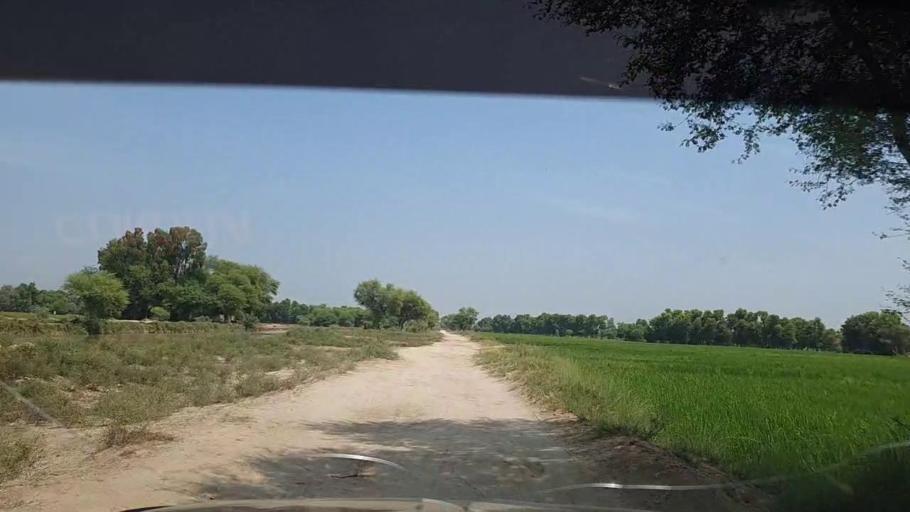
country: PK
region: Sindh
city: Tangwani
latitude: 28.2306
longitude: 68.9340
